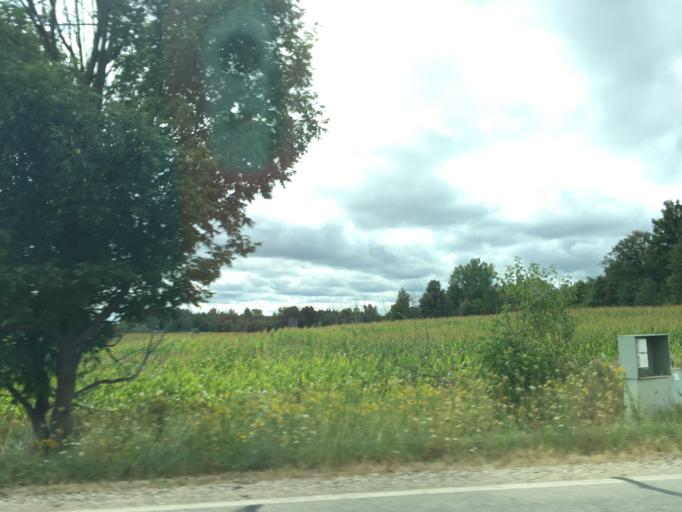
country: US
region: Michigan
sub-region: Lapeer County
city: Barnes Lake-Millers Lake
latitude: 43.3373
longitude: -83.3239
